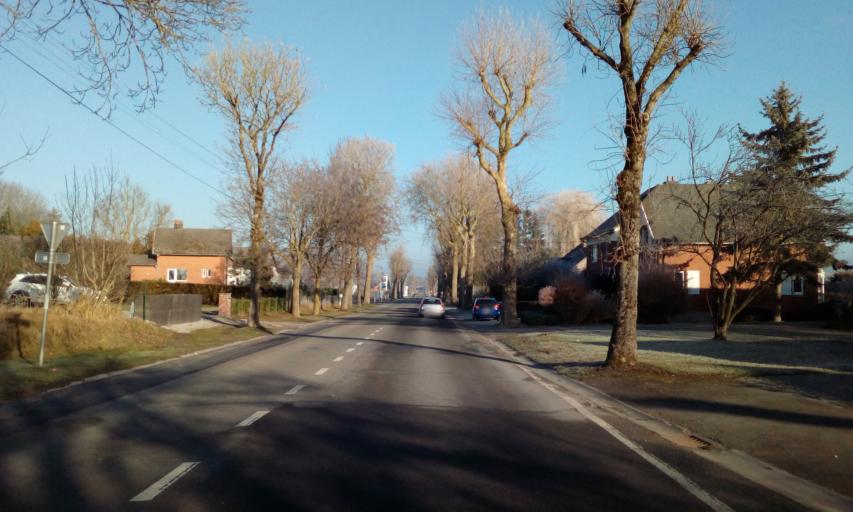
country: BE
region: Wallonia
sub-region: Province de Namur
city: Couvin
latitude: 50.0817
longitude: 4.5153
